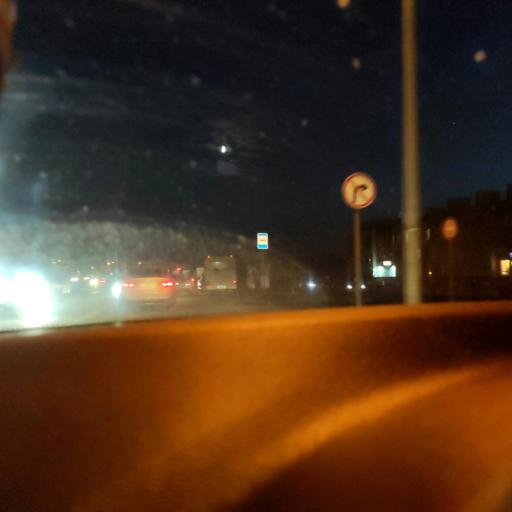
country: RU
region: Samara
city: Petra-Dubrava
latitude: 53.3100
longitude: 50.3095
